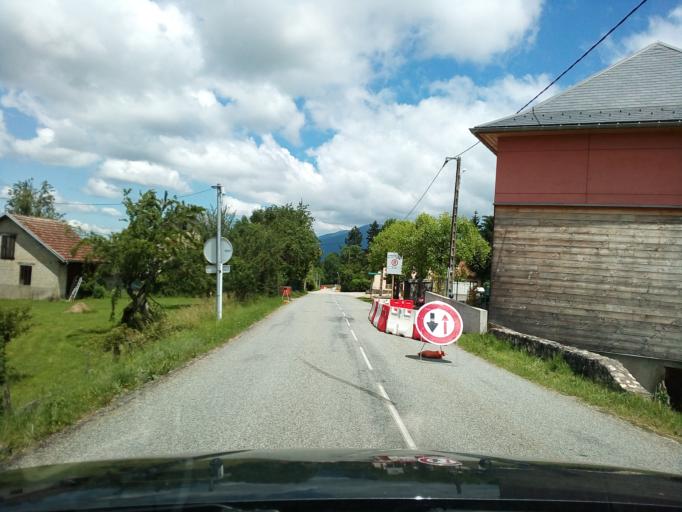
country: FR
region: Rhone-Alpes
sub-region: Departement de la Savoie
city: La Bridoire
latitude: 45.5091
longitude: 5.7702
